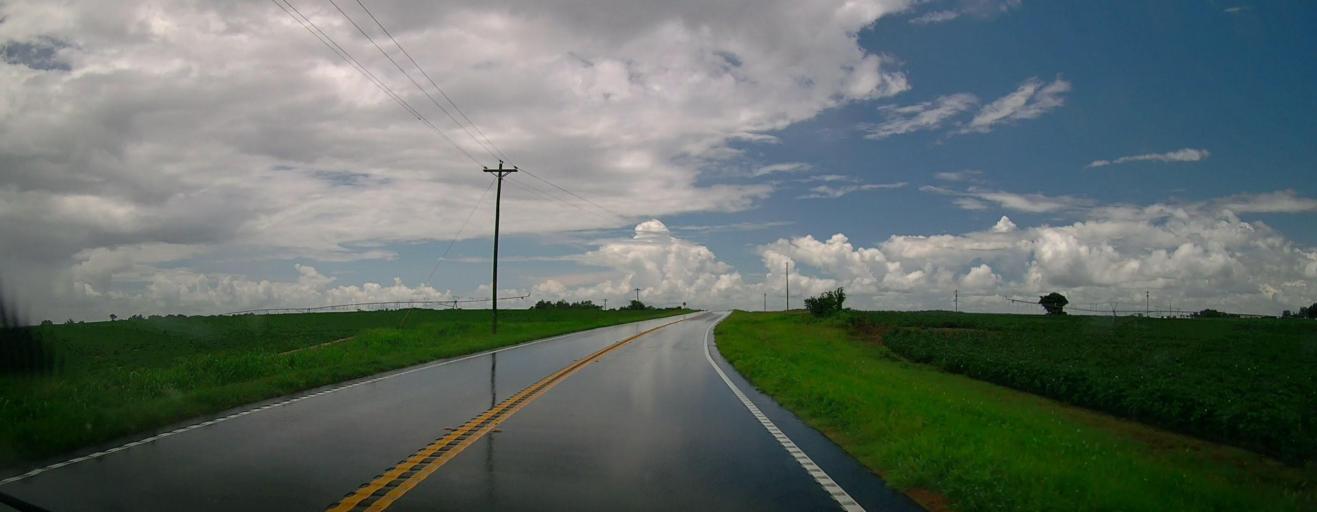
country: US
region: Georgia
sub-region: Pulaski County
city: Hawkinsville
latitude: 32.1887
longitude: -83.5226
